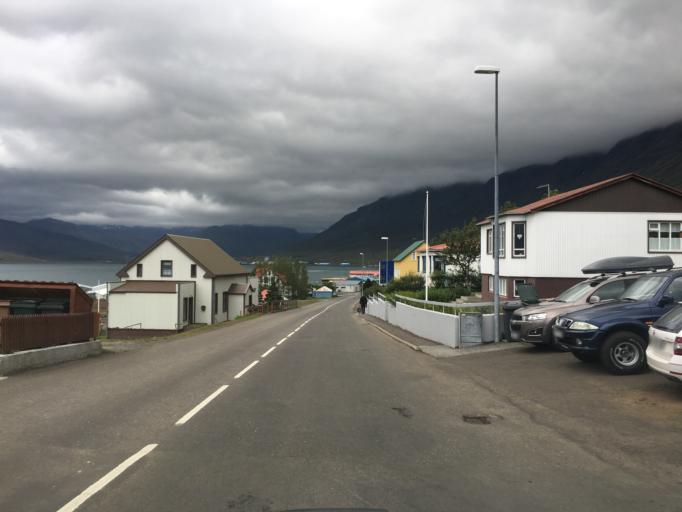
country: IS
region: East
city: Neskaupstadur
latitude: 65.1475
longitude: -13.6736
